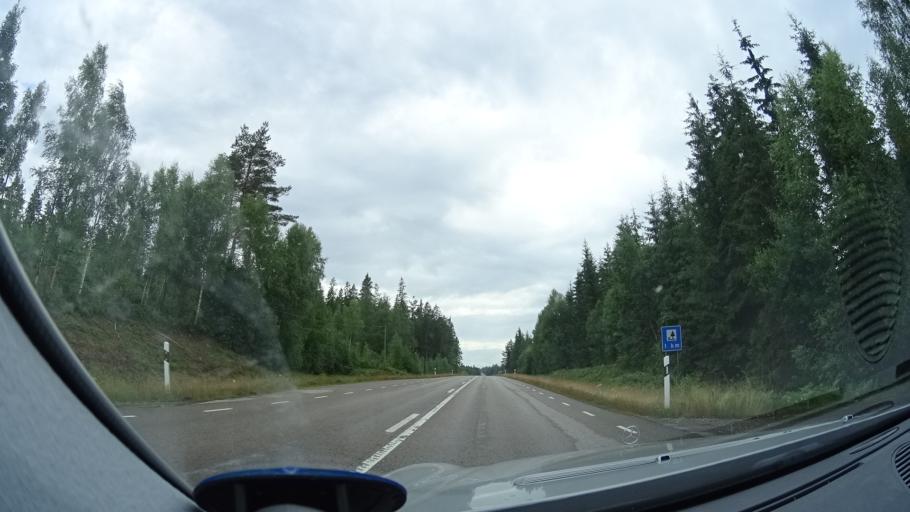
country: SE
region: Kronoberg
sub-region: Tingsryds Kommun
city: Tingsryd
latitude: 56.4483
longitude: 14.9875
